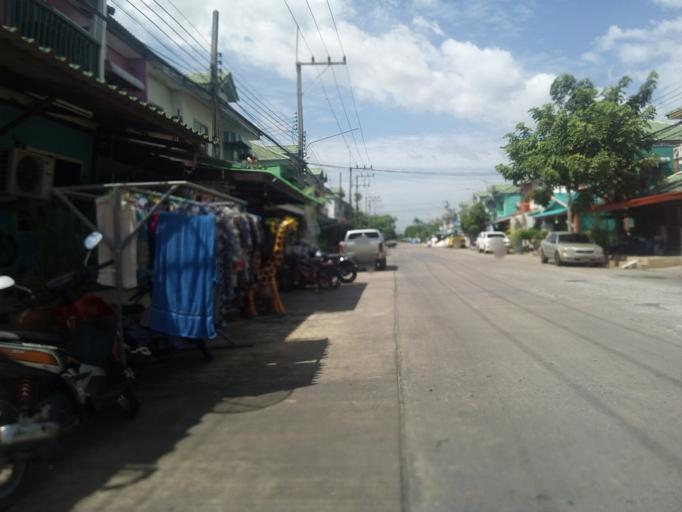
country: TH
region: Pathum Thani
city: Nong Suea
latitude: 14.0555
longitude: 100.8520
